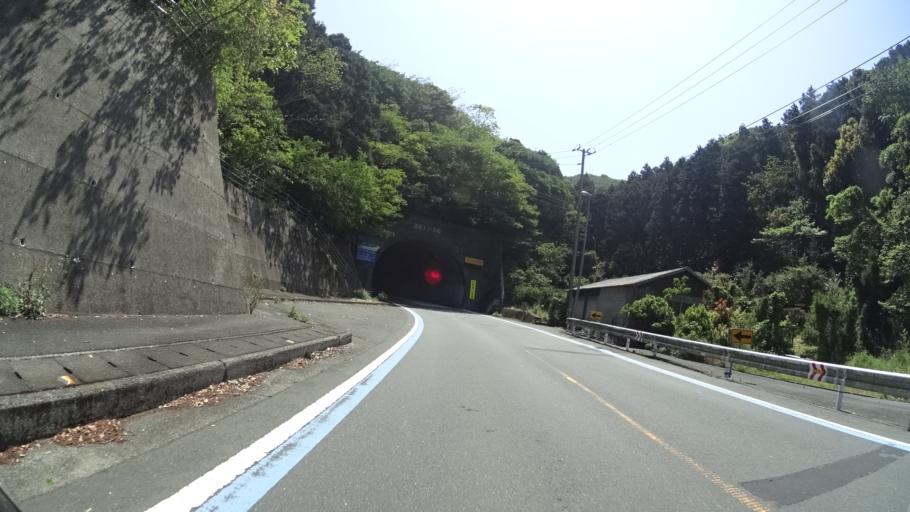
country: JP
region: Ehime
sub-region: Nishiuwa-gun
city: Ikata-cho
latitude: 33.3952
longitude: 132.1514
